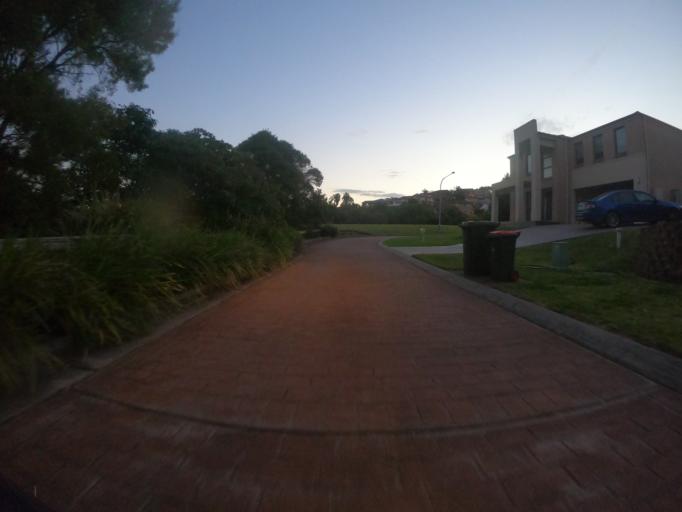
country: AU
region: New South Wales
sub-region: Wollongong
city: Berkeley
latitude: -34.4736
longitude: 150.8530
